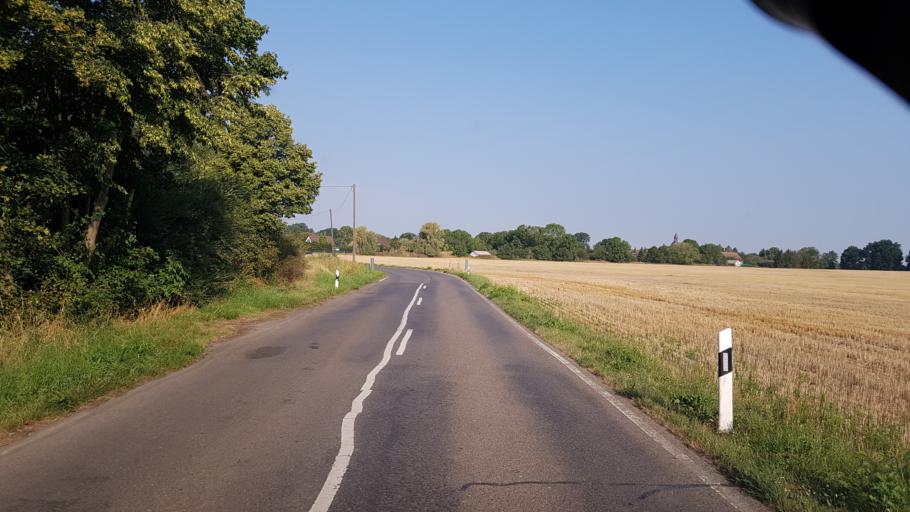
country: DE
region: Brandenburg
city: Drebkau
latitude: 51.6681
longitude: 14.2383
